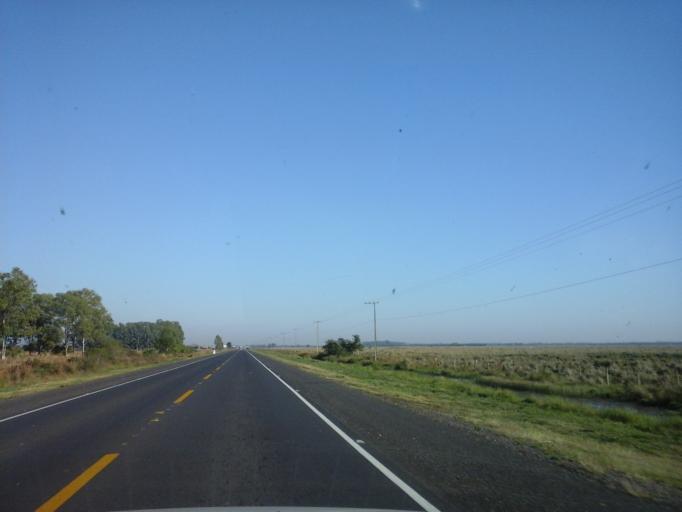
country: PY
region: Neembucu
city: Pilar
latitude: -26.8464
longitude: -58.2497
